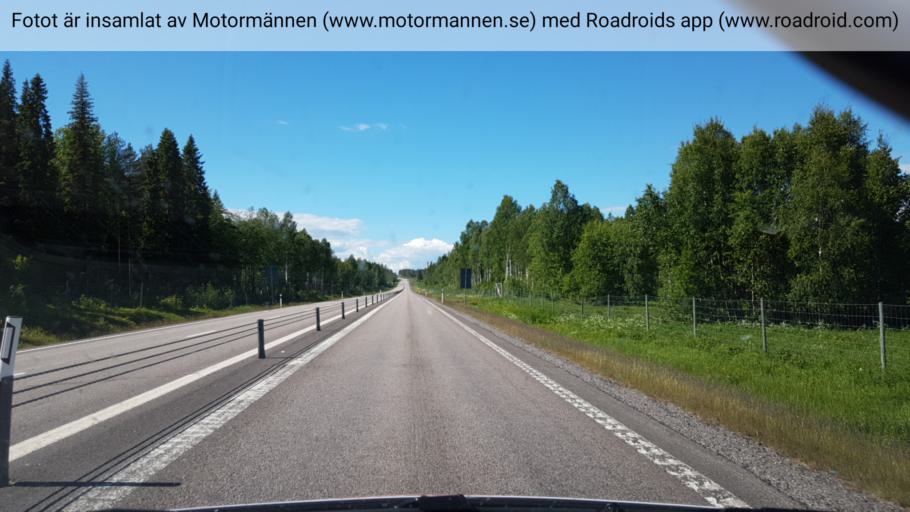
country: SE
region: Norrbotten
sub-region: Kalix Kommun
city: Toere
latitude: 65.8973
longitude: 22.8817
